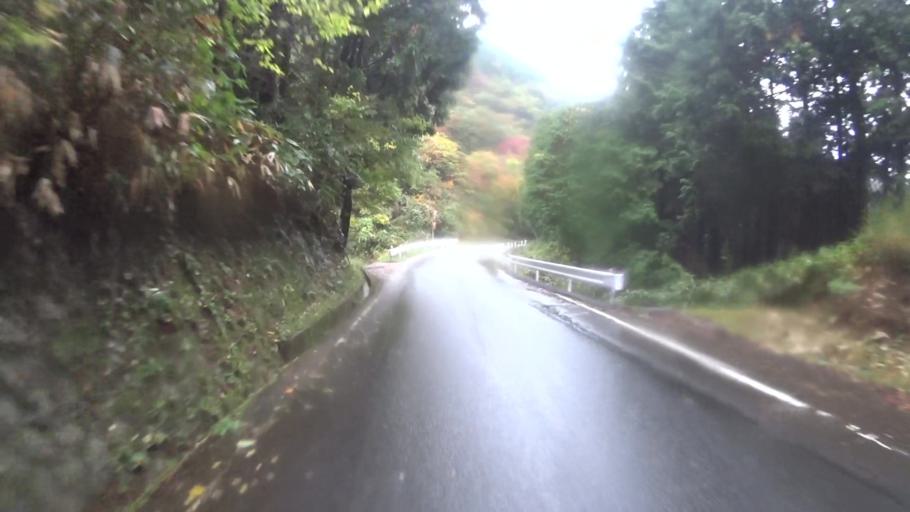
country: JP
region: Kyoto
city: Miyazu
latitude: 35.4820
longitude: 135.1553
